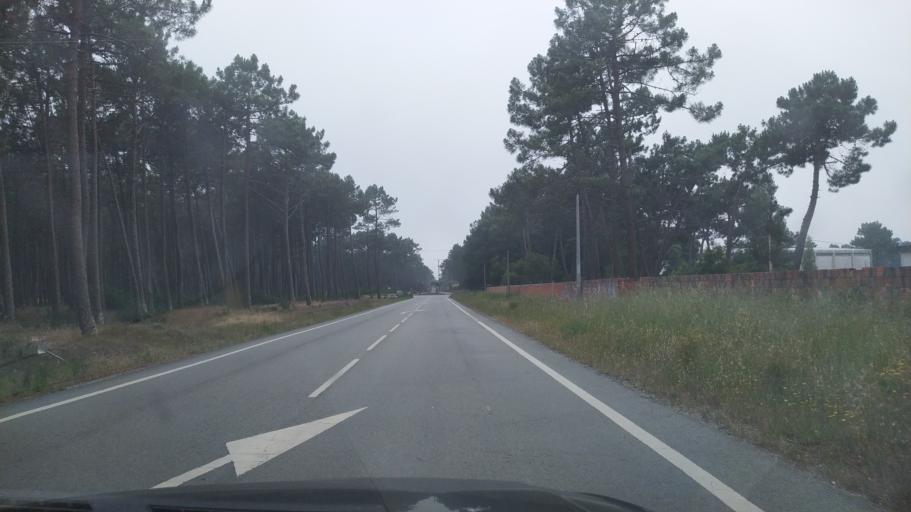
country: PT
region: Aveiro
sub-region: Ilhavo
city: Gafanha da Encarnacao
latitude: 40.5879
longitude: -8.7290
